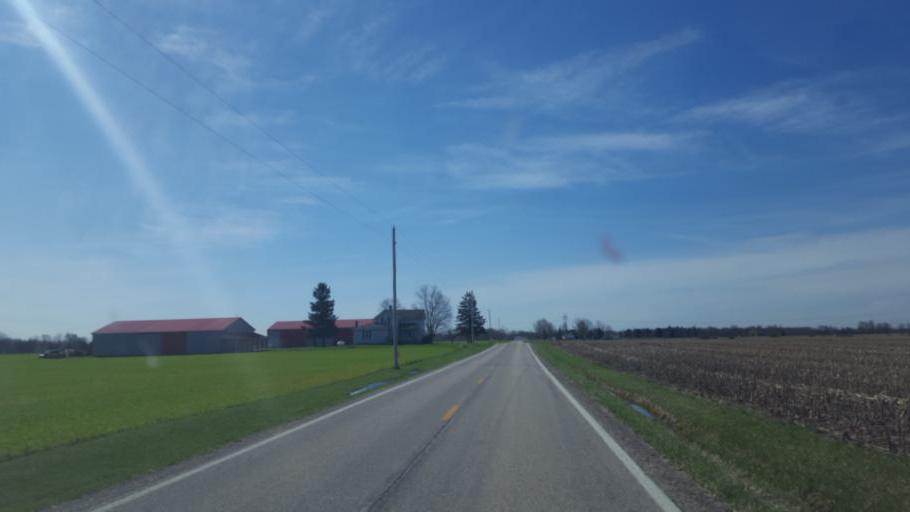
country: US
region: Ohio
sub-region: Morrow County
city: Cardington
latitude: 40.4951
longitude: -82.9632
